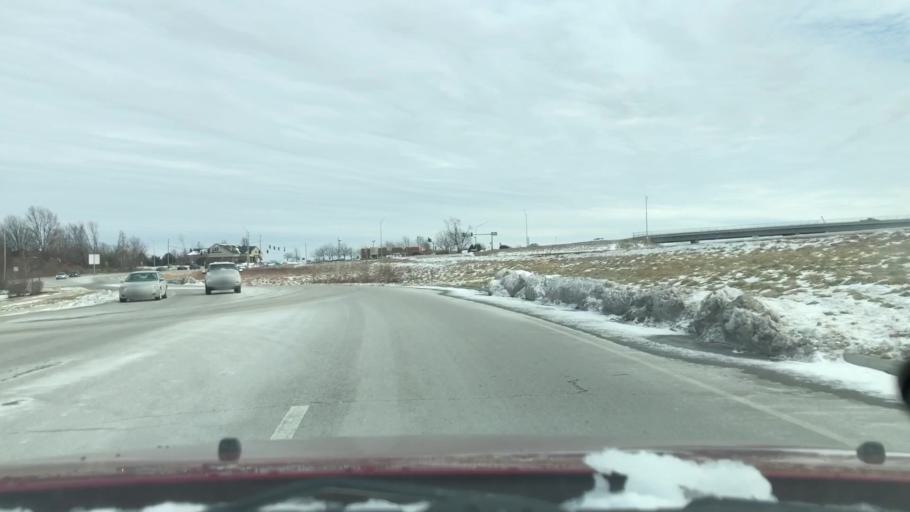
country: US
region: Missouri
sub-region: Jackson County
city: Lees Summit
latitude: 38.9027
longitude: -94.3431
